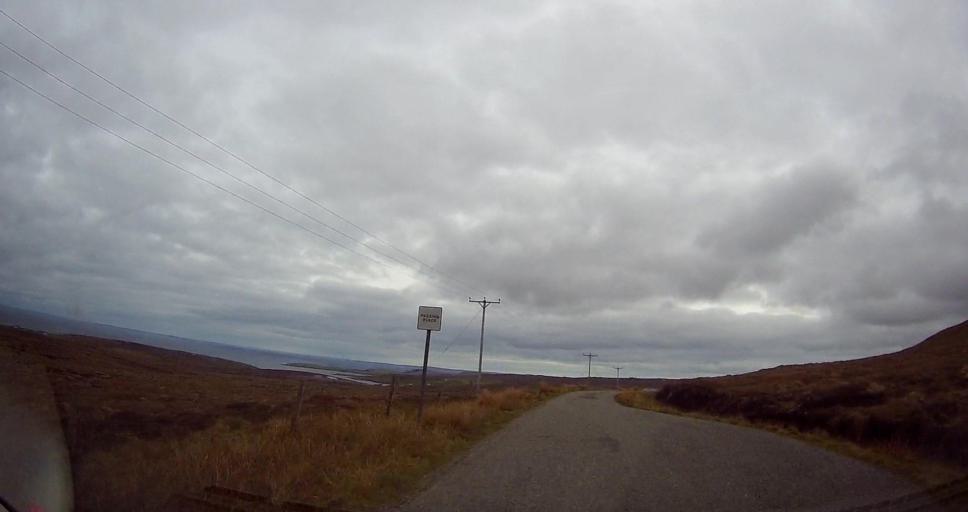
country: GB
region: Scotland
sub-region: Shetland Islands
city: Shetland
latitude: 60.5724
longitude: -1.0666
